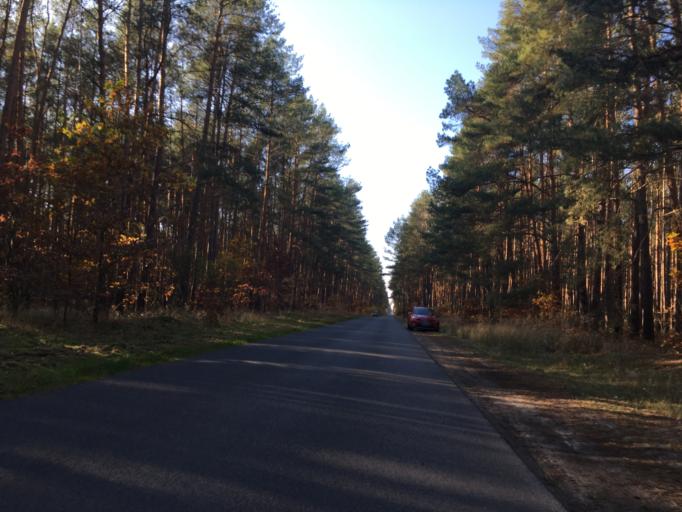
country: DE
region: Brandenburg
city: Spreenhagen
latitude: 52.3432
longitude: 13.9343
